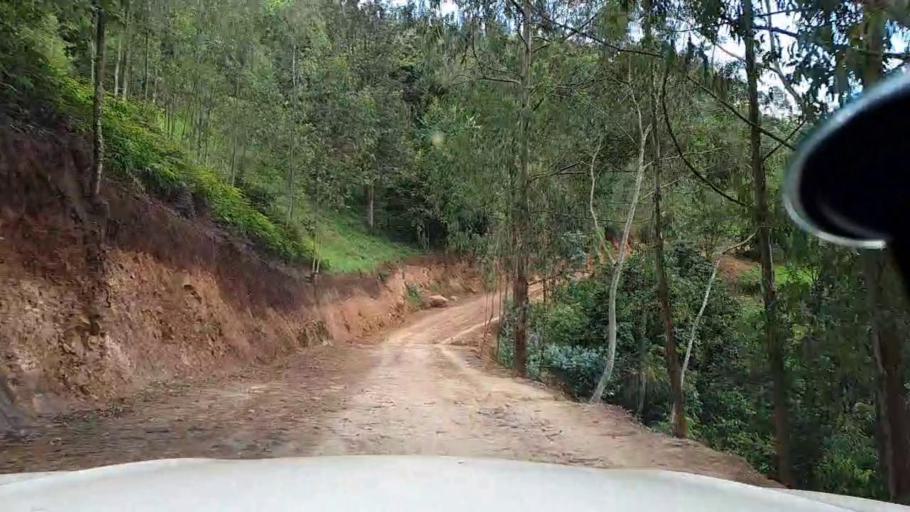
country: RW
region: Southern Province
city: Gitarama
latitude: -1.8069
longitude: 29.7998
